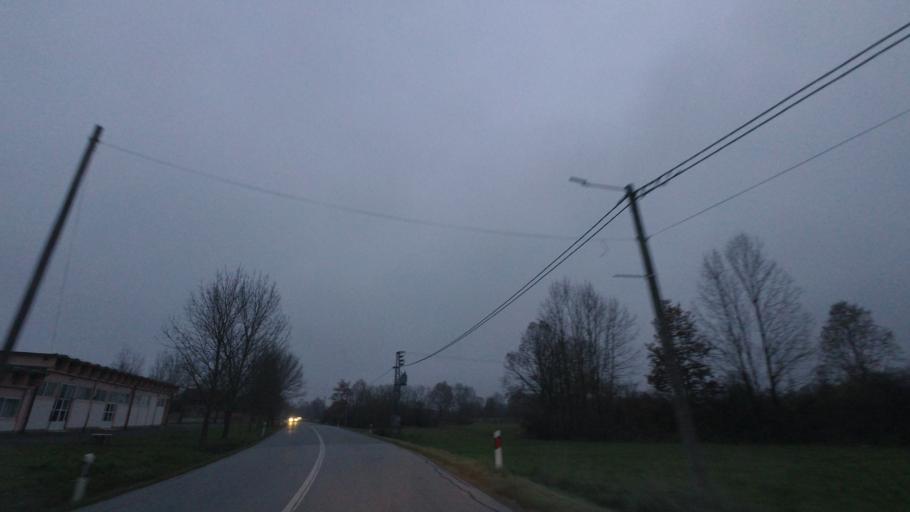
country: HR
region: Sisacko-Moslavacka
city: Glina
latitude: 45.3861
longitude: 16.1407
